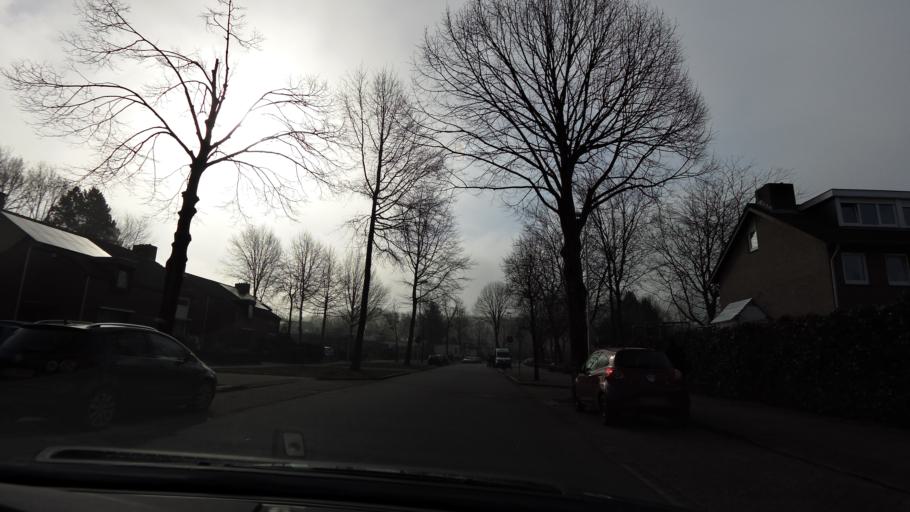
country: NL
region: Limburg
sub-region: Gemeente Heerlen
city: Heerlen
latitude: 50.8733
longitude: 5.9844
